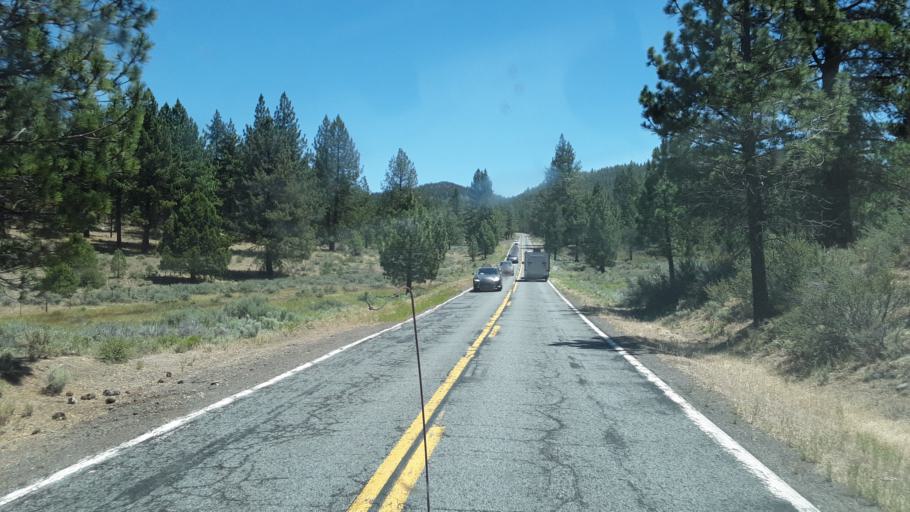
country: US
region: California
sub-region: Modoc County
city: Alturas
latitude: 40.9858
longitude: -120.7976
